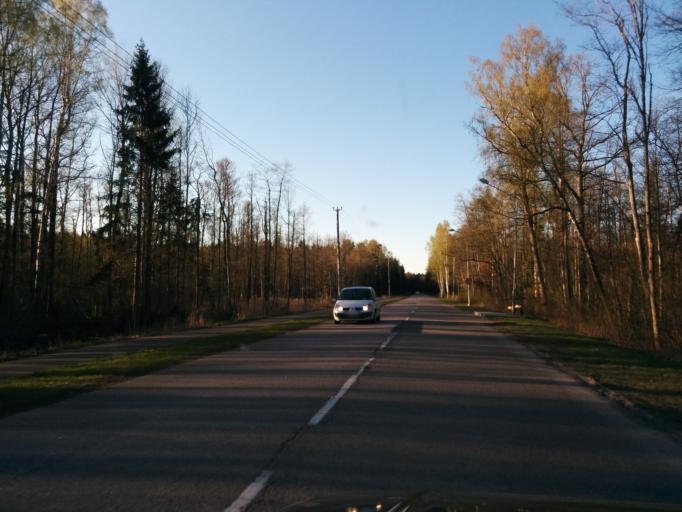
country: LV
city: Tireli
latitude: 56.9532
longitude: 23.5217
